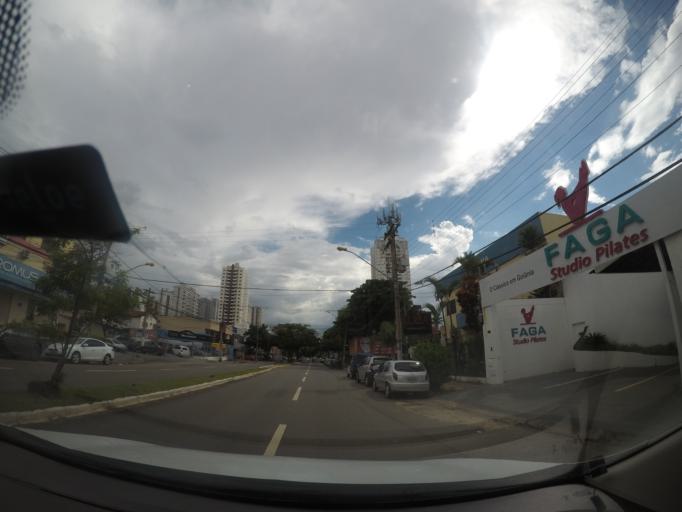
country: BR
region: Goias
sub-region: Goiania
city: Goiania
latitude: -16.6950
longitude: -49.2740
